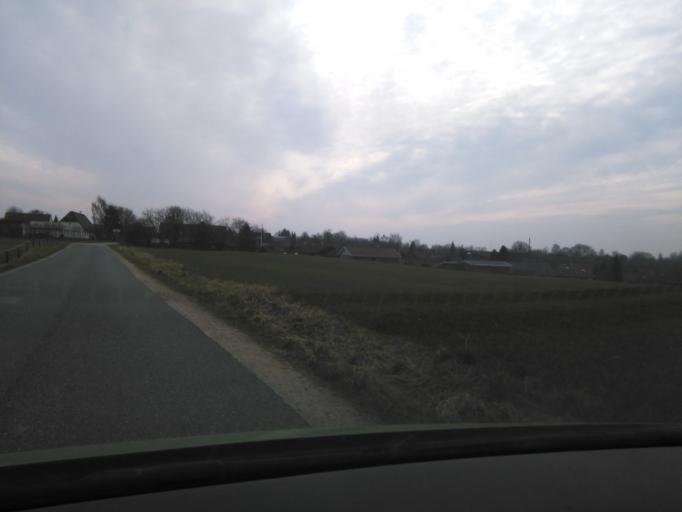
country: DK
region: Central Jutland
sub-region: Arhus Kommune
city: Beder
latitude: 56.0664
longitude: 10.2208
